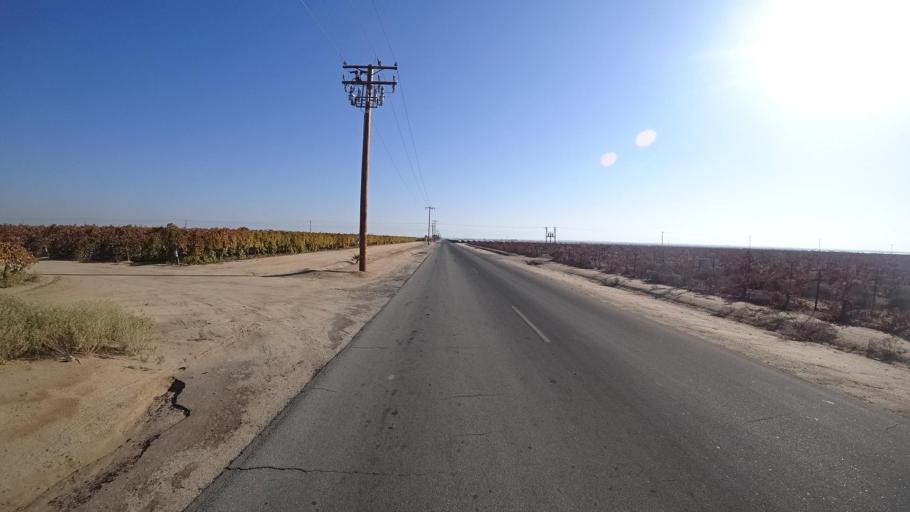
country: US
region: California
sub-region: Kern County
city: Delano
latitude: 35.7475
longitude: -119.1715
